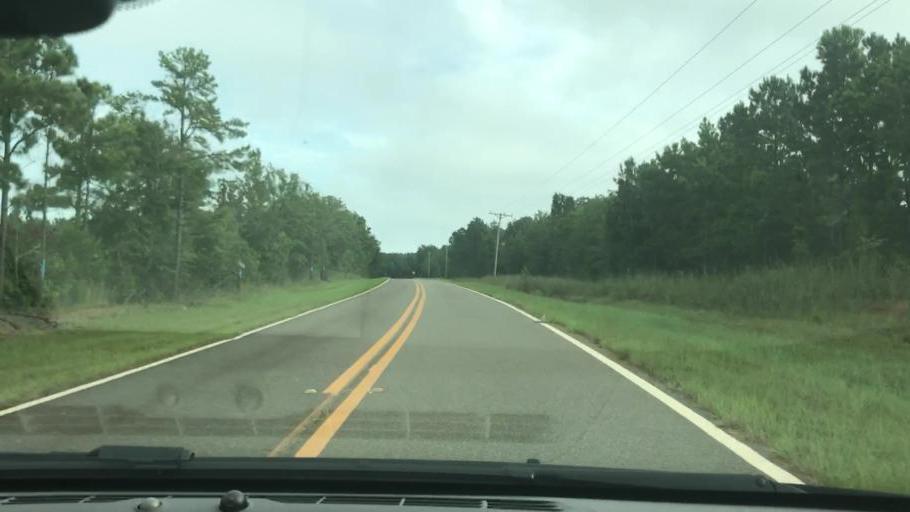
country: US
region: Georgia
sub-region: Stewart County
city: Lumpkin
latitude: 32.0383
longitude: -84.9096
